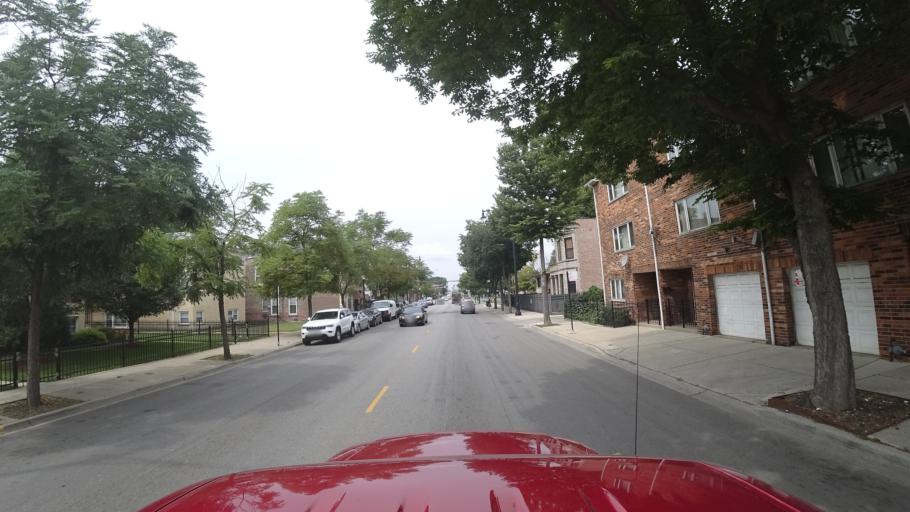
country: US
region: Illinois
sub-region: Cook County
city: Chicago
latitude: 41.8303
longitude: -87.6828
